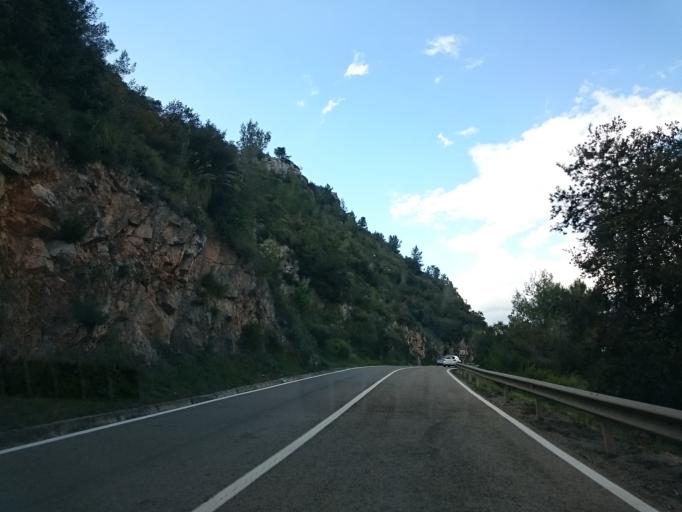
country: ES
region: Catalonia
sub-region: Provincia de Barcelona
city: Begues
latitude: 41.3235
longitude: 1.9493
